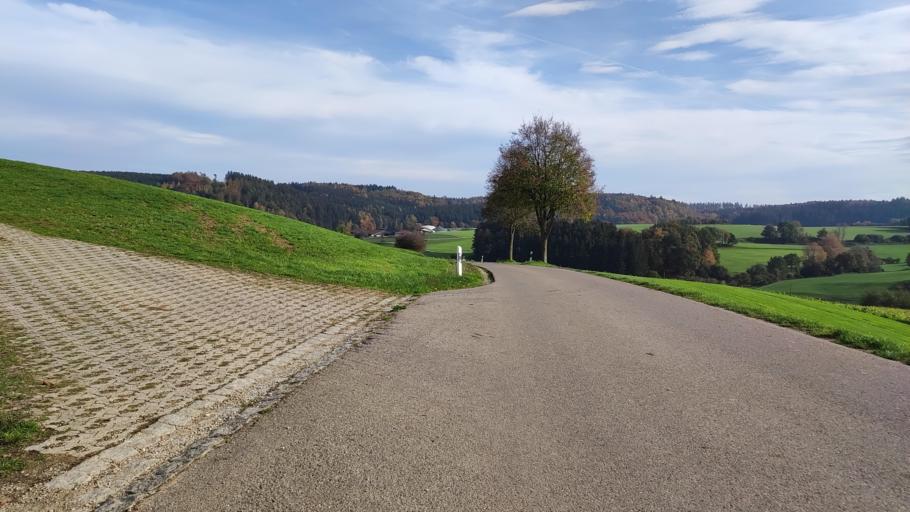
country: DE
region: Bavaria
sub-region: Swabia
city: Ziemetshausen
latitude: 48.2869
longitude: 10.5534
